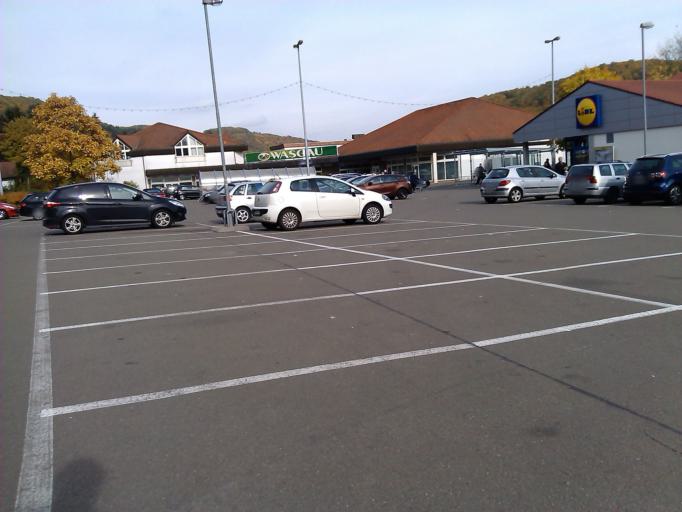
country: DE
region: Rheinland-Pfalz
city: Lauterecken
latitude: 49.6557
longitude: 7.5908
